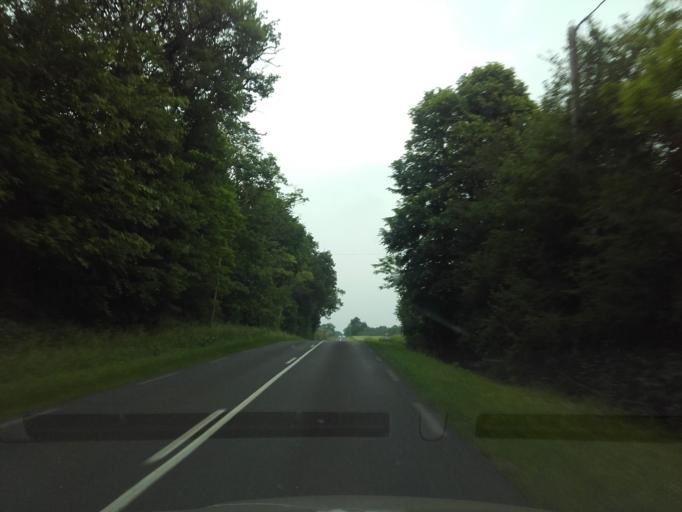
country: FR
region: Centre
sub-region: Departement d'Indre-et-Loire
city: Beaumont-la-Ronce
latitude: 47.6054
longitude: 0.6615
